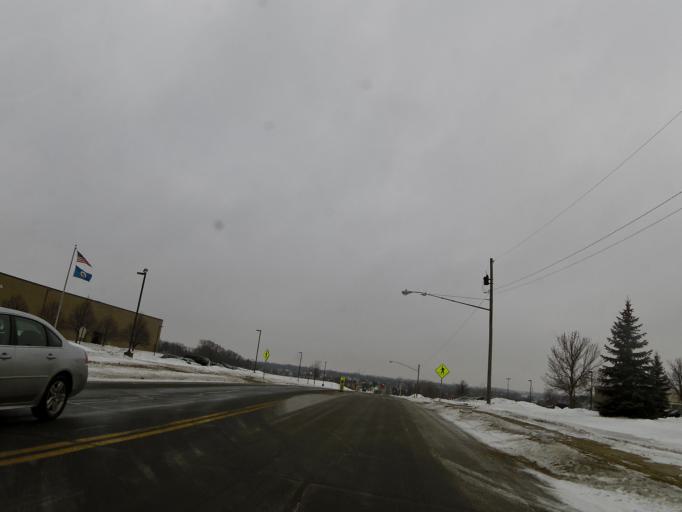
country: US
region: Minnesota
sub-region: Scott County
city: Prior Lake
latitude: 44.7201
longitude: -93.4039
